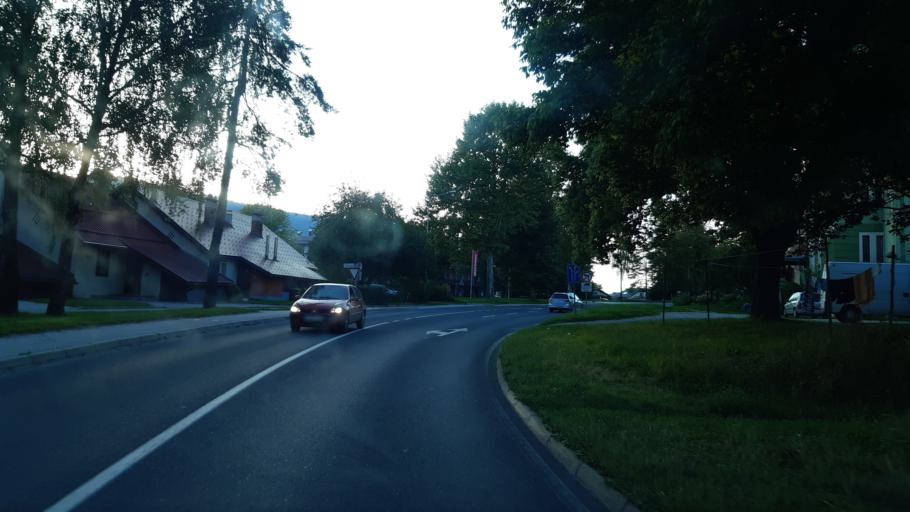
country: SI
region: Kocevje
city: Kocevje
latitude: 45.6437
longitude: 14.8586
